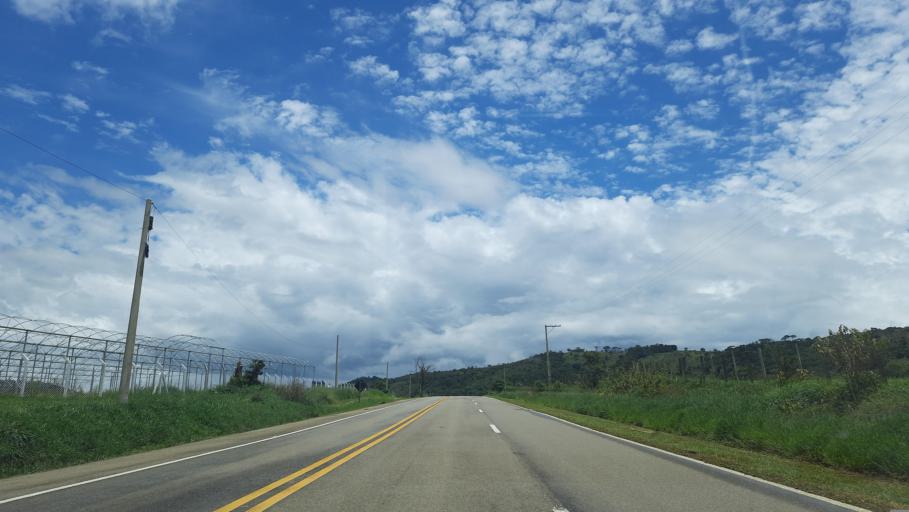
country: BR
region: Sao Paulo
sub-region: Vargem Grande Do Sul
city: Vargem Grande do Sul
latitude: -21.8224
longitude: -46.7826
